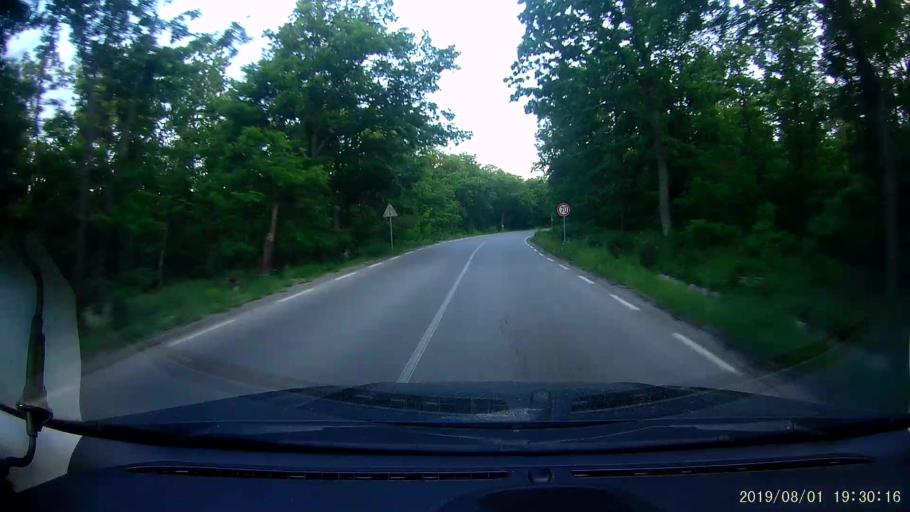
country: BG
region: Burgas
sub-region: Obshtina Sungurlare
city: Sungurlare
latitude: 42.8161
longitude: 26.8943
